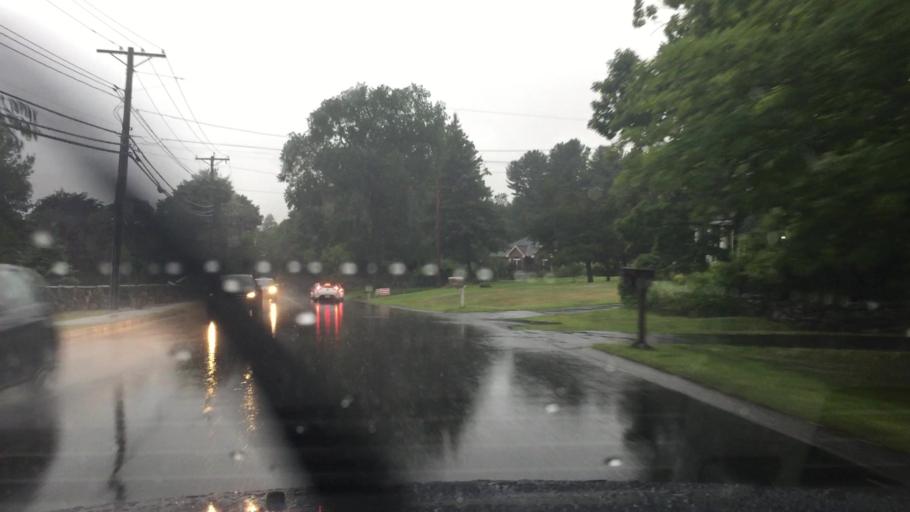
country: US
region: Massachusetts
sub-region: Middlesex County
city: Tewksbury
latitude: 42.6427
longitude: -71.2537
